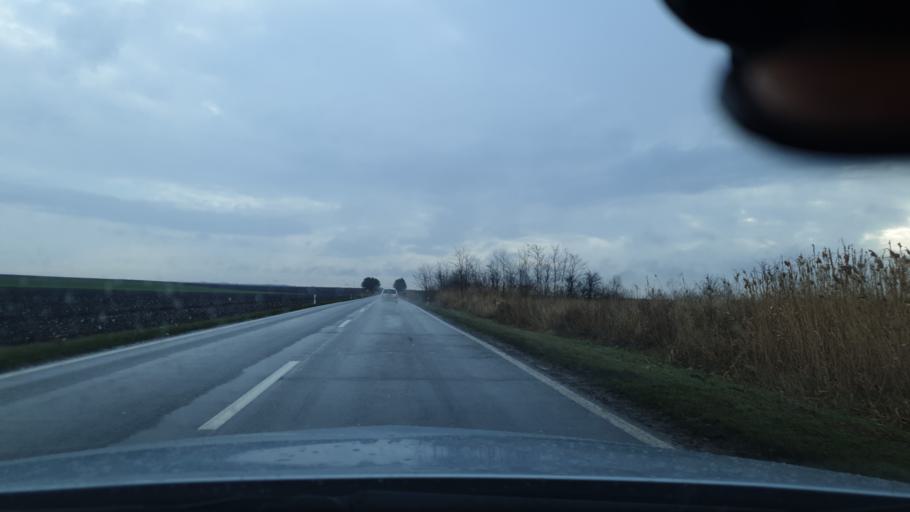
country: RS
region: Autonomna Pokrajina Vojvodina
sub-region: Juznobanatski Okrug
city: Kovin
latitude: 44.8334
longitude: 20.8230
